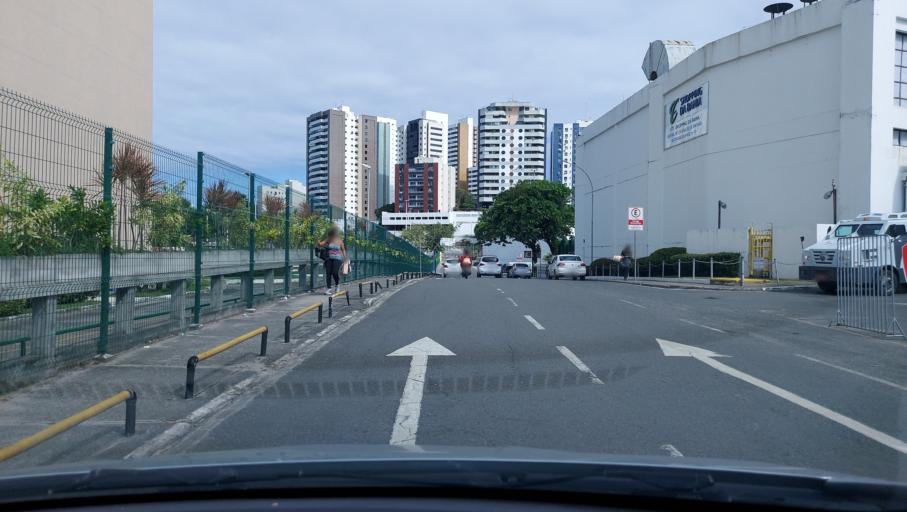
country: BR
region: Bahia
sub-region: Salvador
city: Salvador
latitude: -12.9807
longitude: -38.4634
